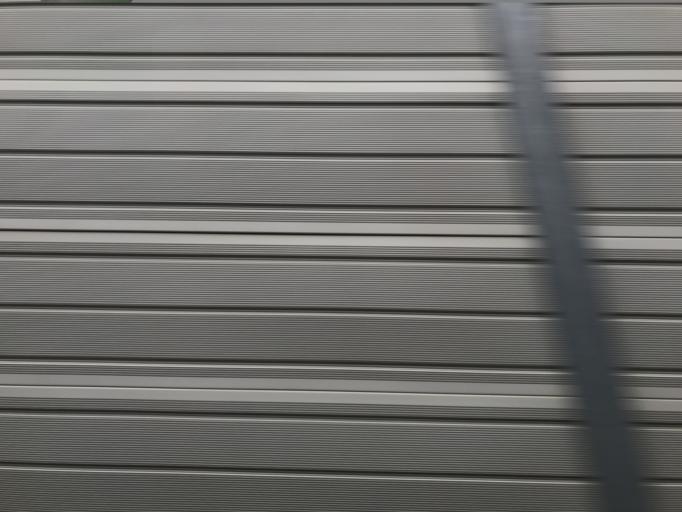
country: TR
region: Istanbul
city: Pendik
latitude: 40.8742
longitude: 29.2501
